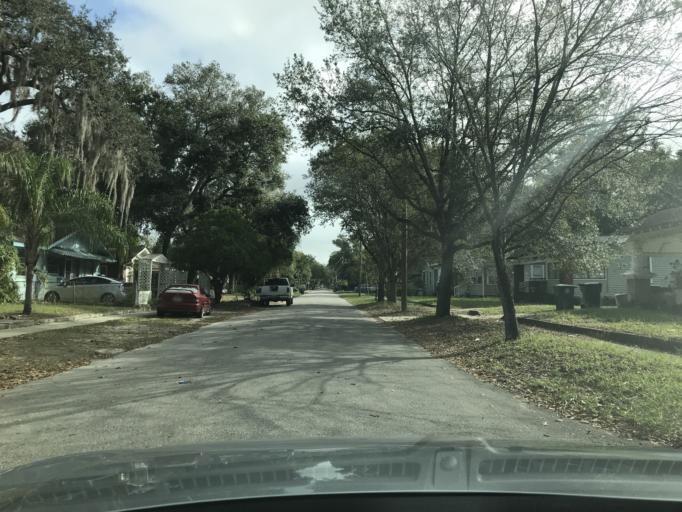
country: US
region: Florida
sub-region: Hillsborough County
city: Egypt Lake-Leto
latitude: 27.9988
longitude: -82.4615
